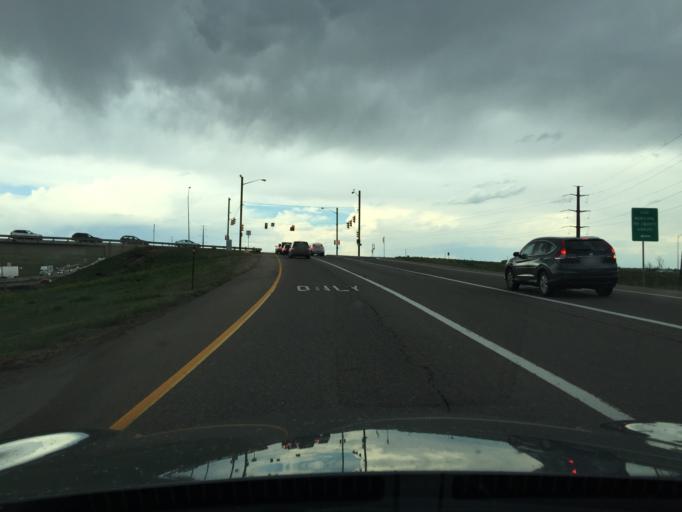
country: US
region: Colorado
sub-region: Boulder County
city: Erie
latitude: 39.9994
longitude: -104.9806
